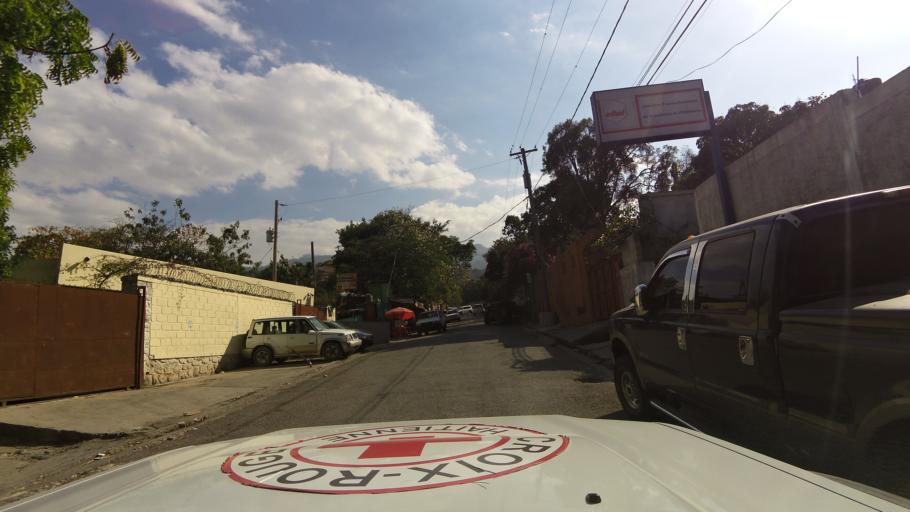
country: HT
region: Ouest
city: Petionville
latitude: 18.5151
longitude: -72.2807
